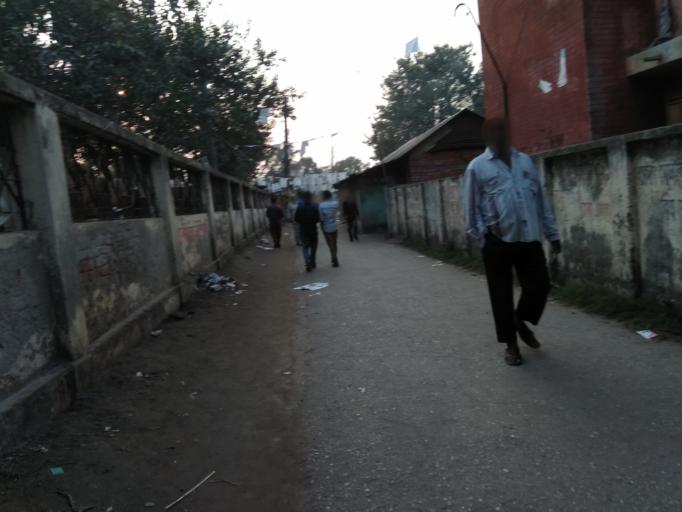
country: BD
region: Rangpur Division
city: Rangpur
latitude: 25.7288
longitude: 89.2633
